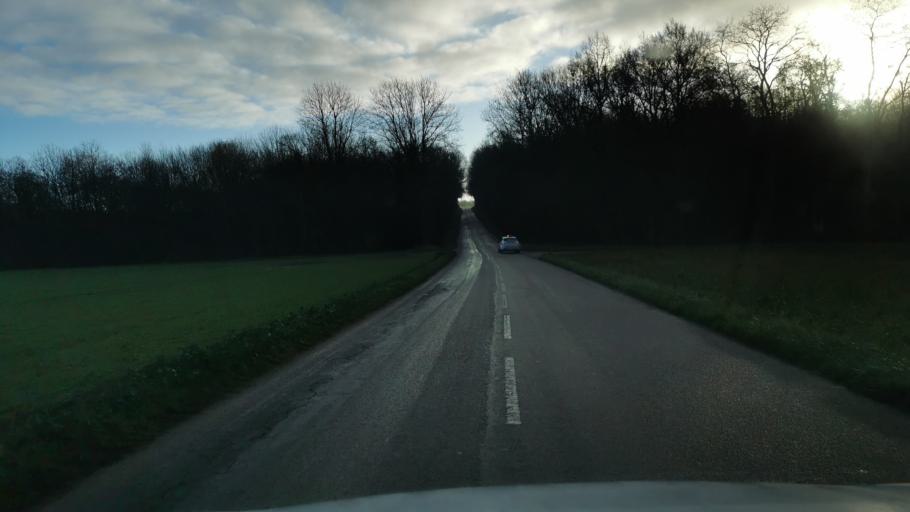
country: FR
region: Ile-de-France
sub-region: Departement des Yvelines
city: Houdan
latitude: 48.8335
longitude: 1.6171
